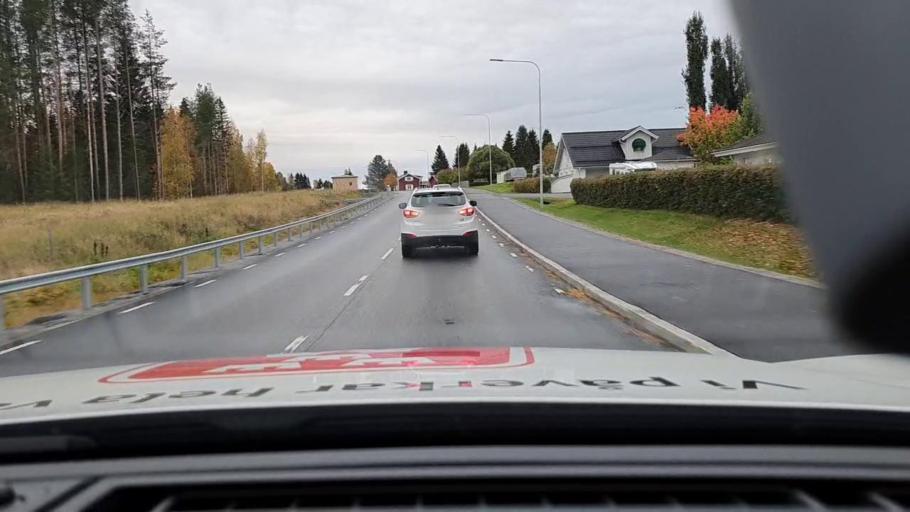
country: SE
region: Norrbotten
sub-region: Bodens Kommun
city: Saevast
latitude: 65.7758
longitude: 21.6943
